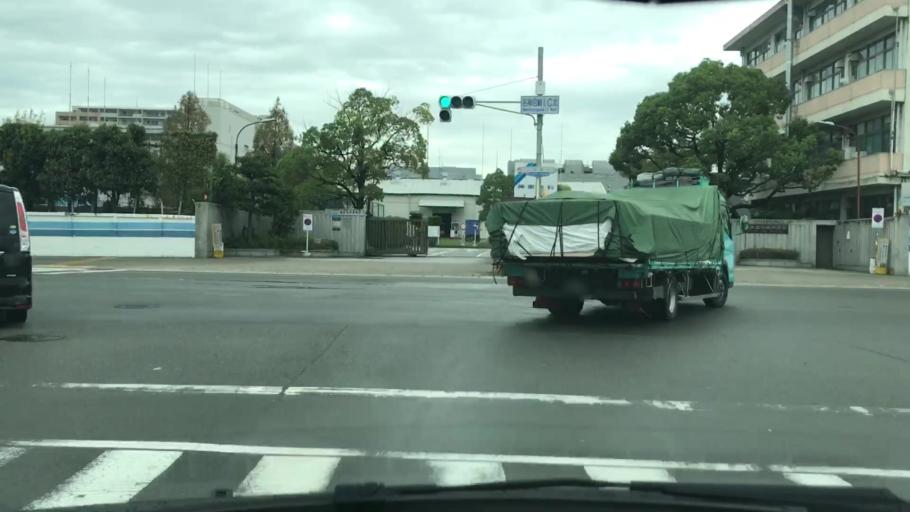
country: JP
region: Hyogo
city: Amagasaki
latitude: 34.7436
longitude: 135.4153
